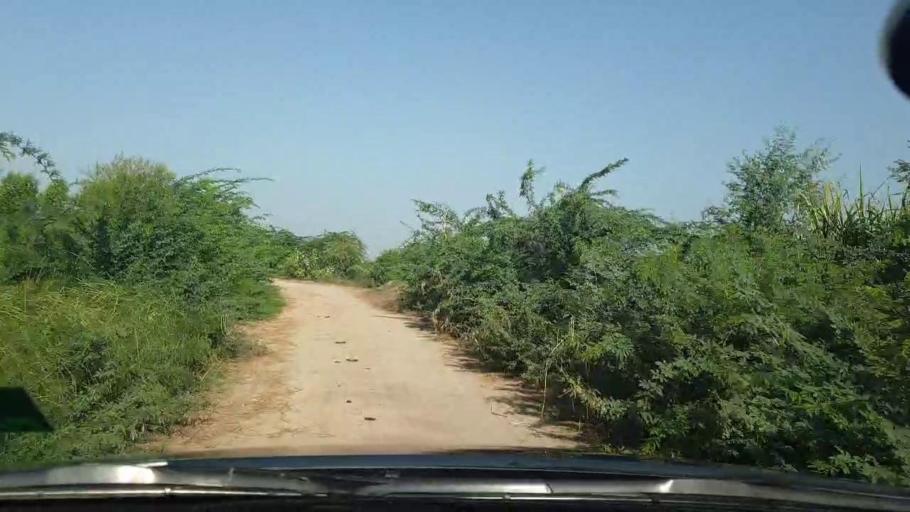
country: PK
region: Sindh
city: Tando Bago
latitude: 24.6853
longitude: 69.0148
